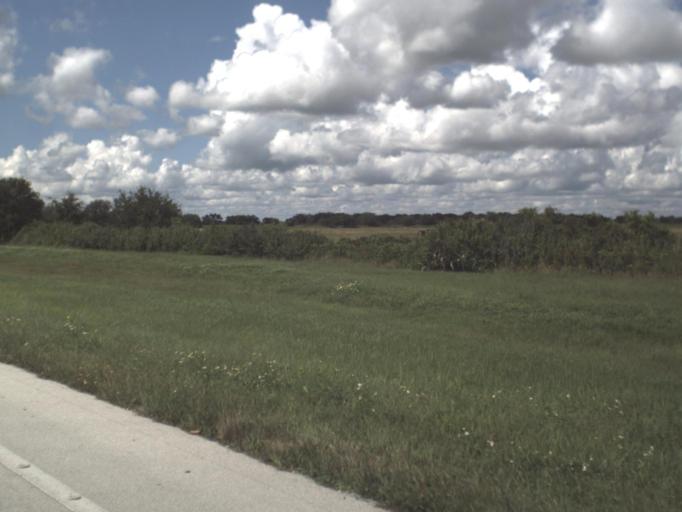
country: US
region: Florida
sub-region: DeSoto County
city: Southeast Arcadia
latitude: 27.2095
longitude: -81.7018
